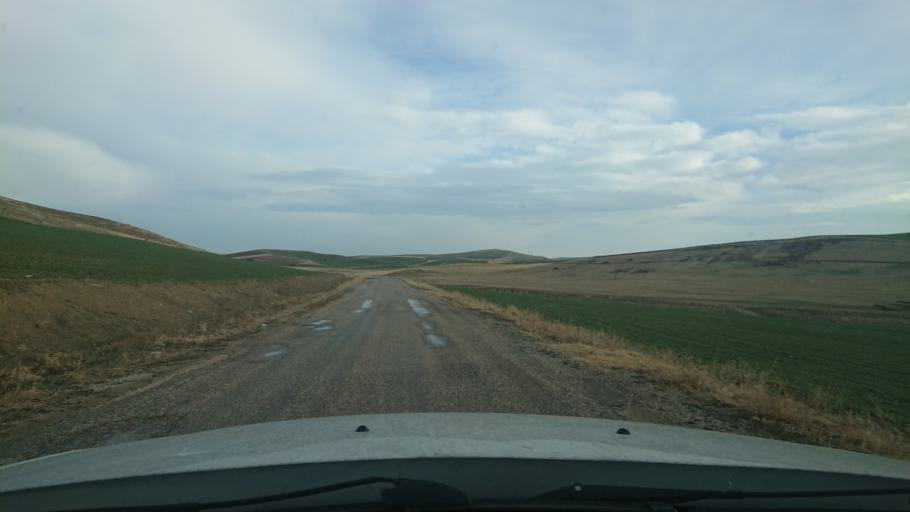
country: TR
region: Aksaray
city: Acipinar
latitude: 38.6389
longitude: 33.8067
